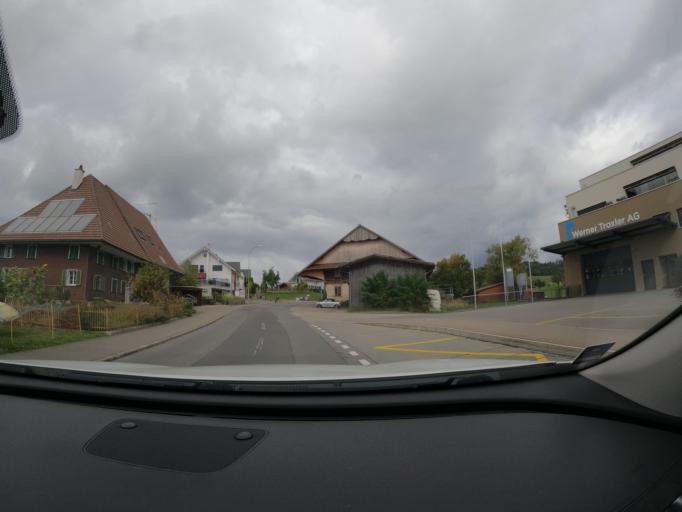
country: CH
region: Lucerne
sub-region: Sursee District
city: Bueron
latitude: 47.2243
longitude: 8.1121
